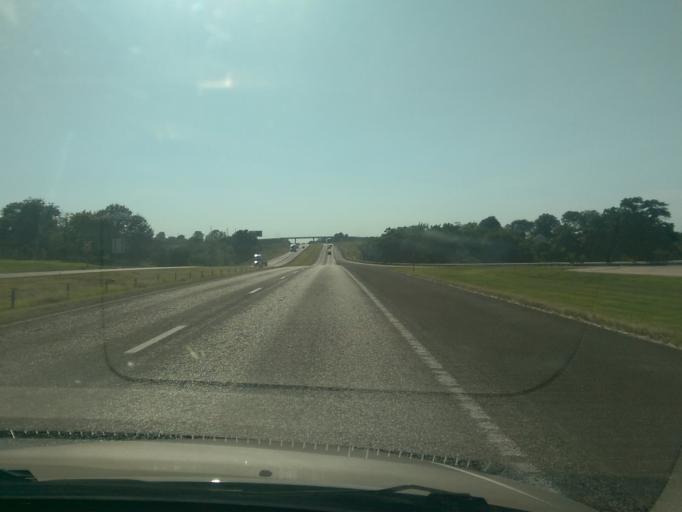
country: US
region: Missouri
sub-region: Lafayette County
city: Concordia
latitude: 38.9938
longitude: -93.5872
